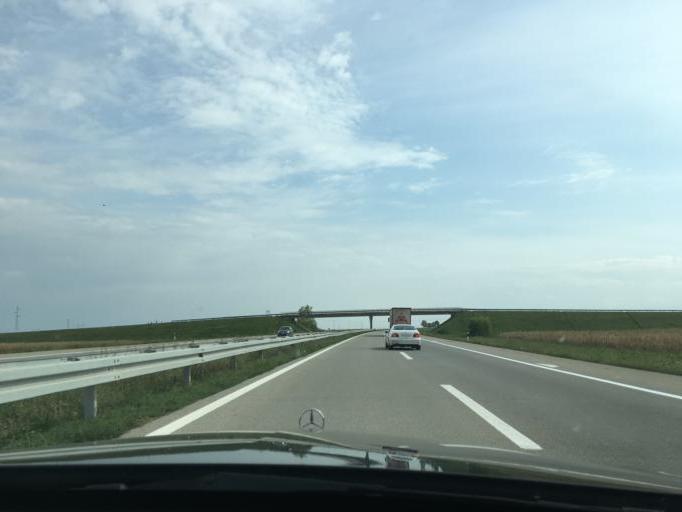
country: RS
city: Ravnje
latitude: 45.0426
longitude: 19.4269
